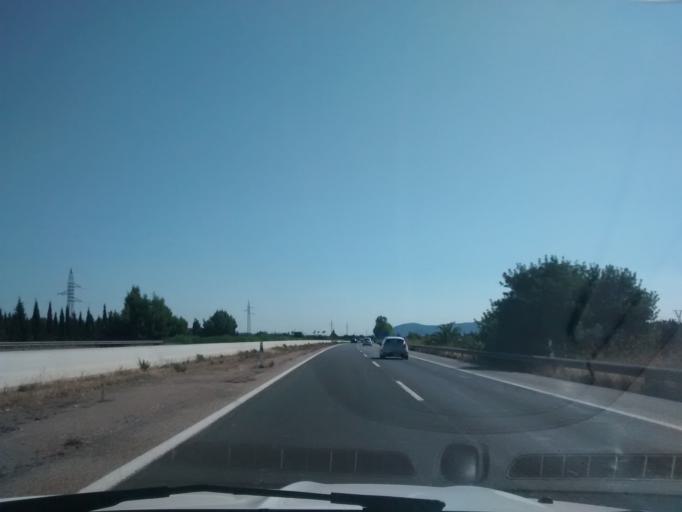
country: ES
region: Balearic Islands
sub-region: Illes Balears
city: Lloseta
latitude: 39.6970
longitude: 2.8819
